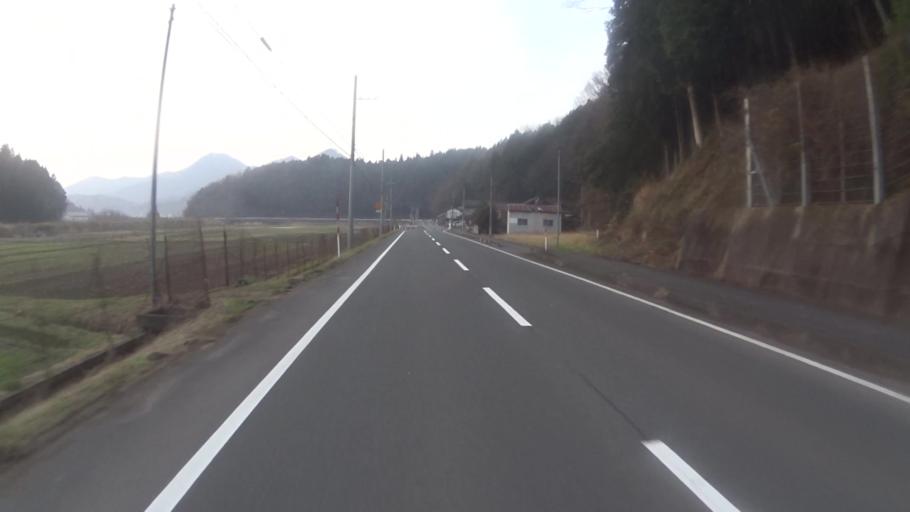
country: JP
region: Kyoto
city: Maizuru
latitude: 35.3673
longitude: 135.4312
